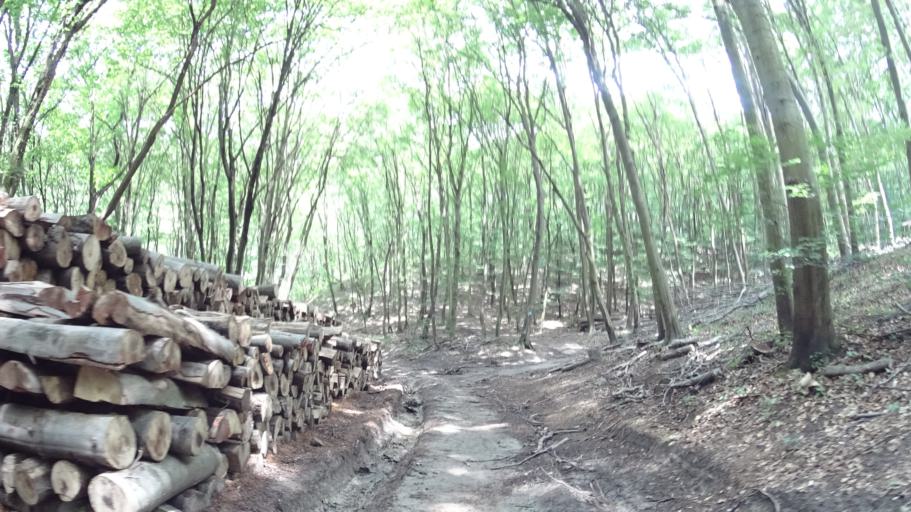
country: HU
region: Pest
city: Nagymaros
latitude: 47.7988
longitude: 18.9170
